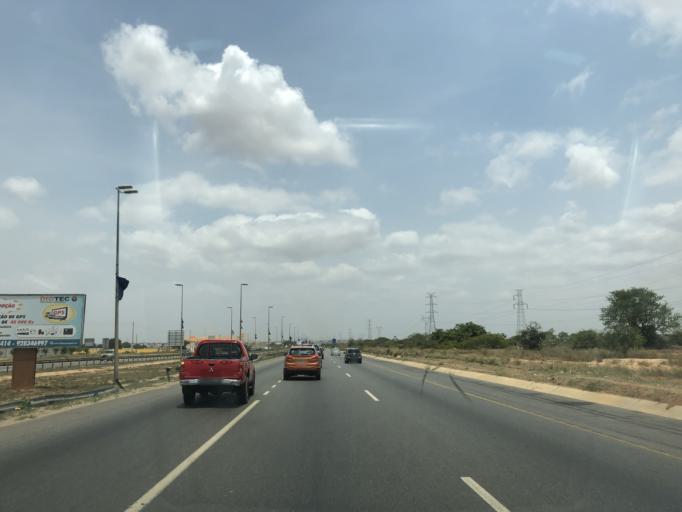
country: AO
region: Luanda
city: Luanda
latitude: -8.9735
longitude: 13.2634
